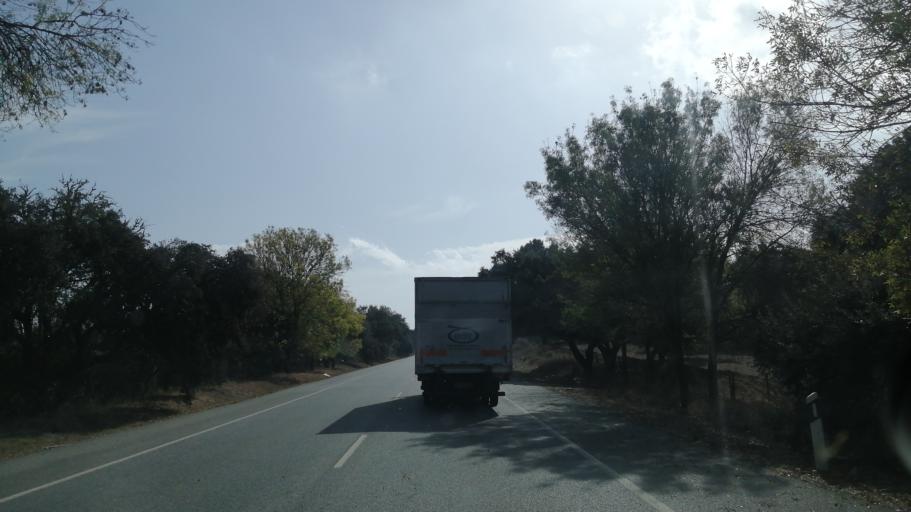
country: PT
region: Evora
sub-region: Montemor-O-Novo
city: Montemor-o-Novo
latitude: 38.6288
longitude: -8.1128
